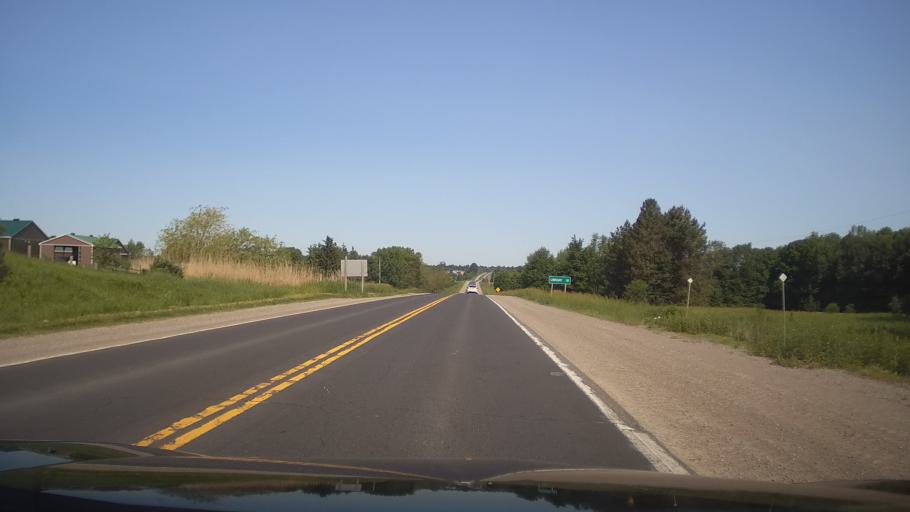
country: CA
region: Ontario
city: Omemee
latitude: 44.2943
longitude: -78.5948
